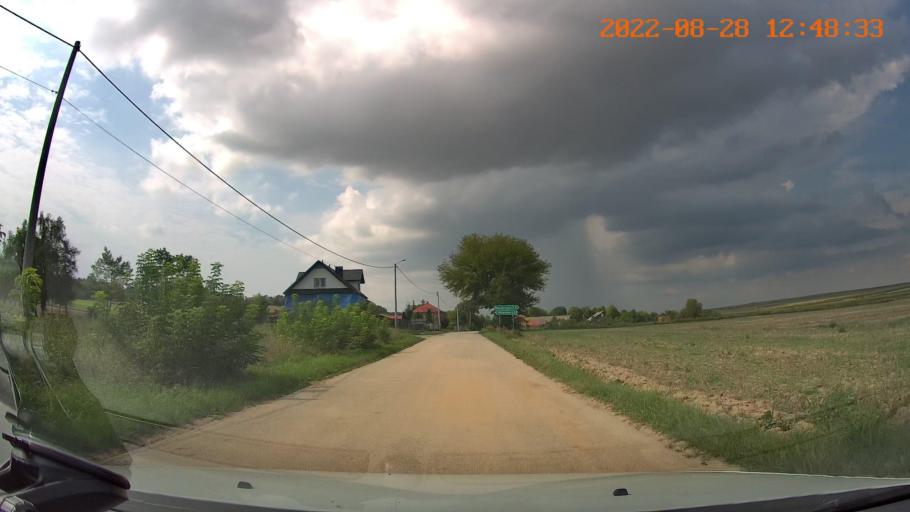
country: PL
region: Swietokrzyskie
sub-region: Powiat pinczowski
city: Dzialoszyce
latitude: 50.3582
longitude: 20.2908
